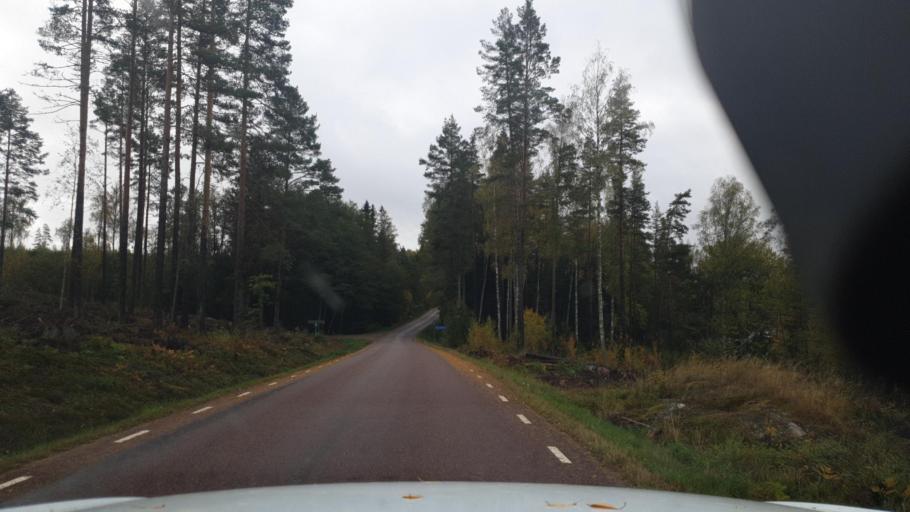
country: SE
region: Vaermland
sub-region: Grums Kommun
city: Grums
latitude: 59.4229
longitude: 13.0867
